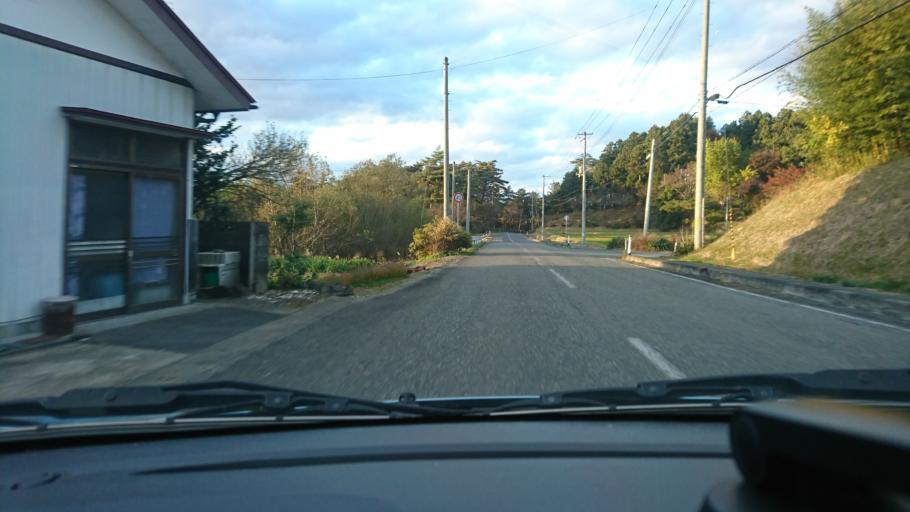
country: JP
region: Iwate
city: Ichinoseki
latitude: 38.8014
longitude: 141.1931
